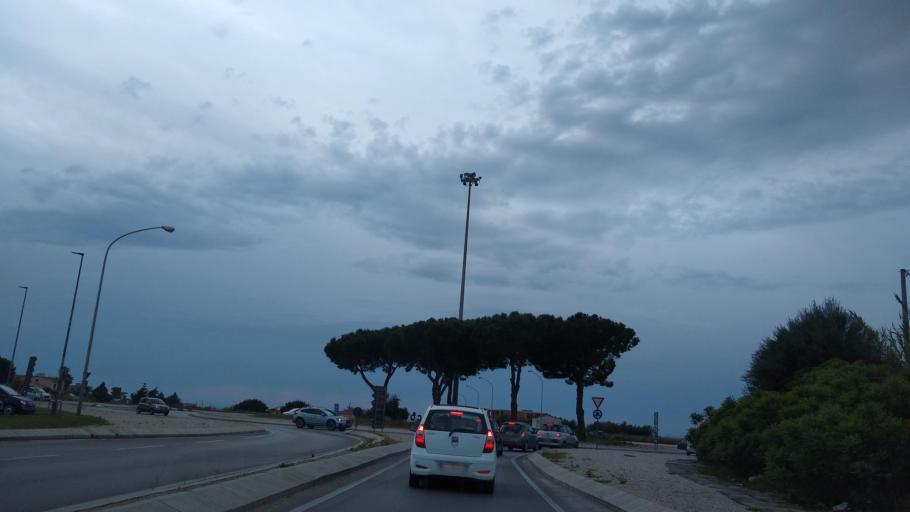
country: IT
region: Sicily
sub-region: Palermo
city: Partinico
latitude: 38.0391
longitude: 13.1085
